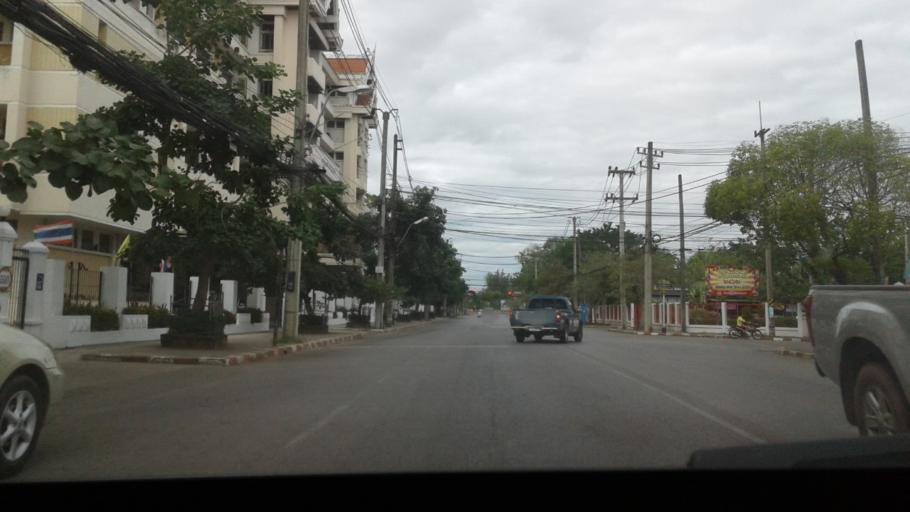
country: TH
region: Changwat Udon Thani
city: Udon Thani
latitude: 17.4155
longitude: 102.7883
